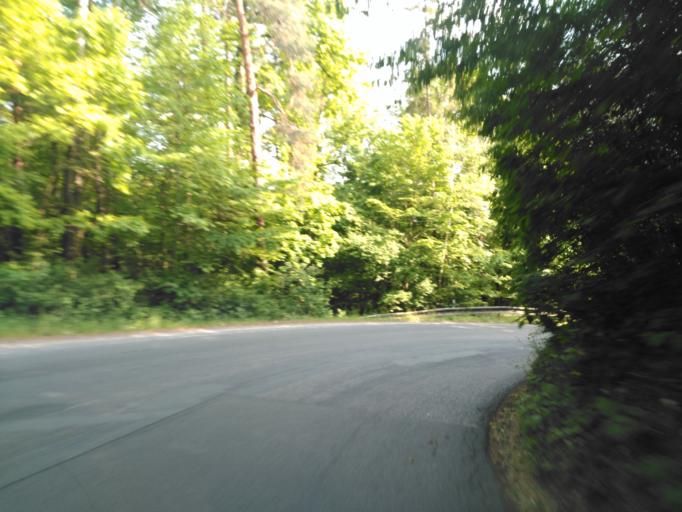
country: CZ
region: Central Bohemia
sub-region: Okres Beroun
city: Beroun
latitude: 49.9822
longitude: 14.0782
